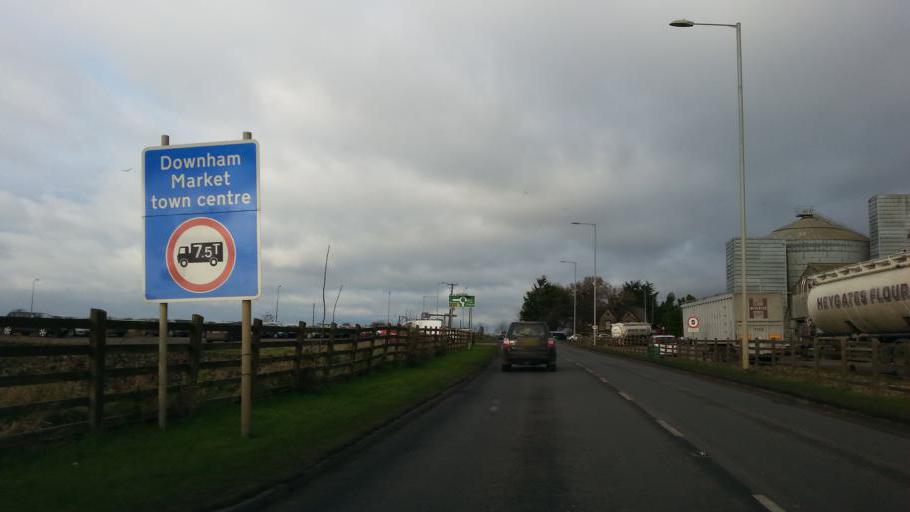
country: GB
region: England
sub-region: Norfolk
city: Downham Market
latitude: 52.6023
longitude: 0.3635
